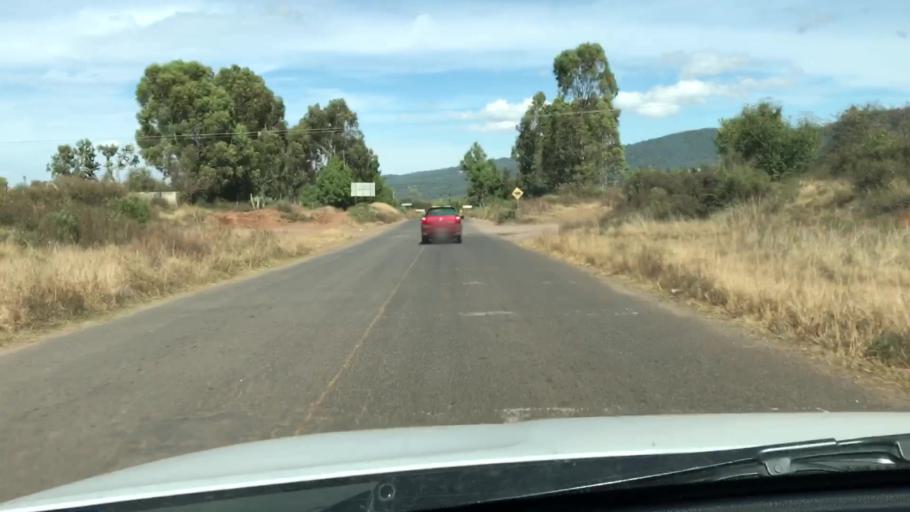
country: MX
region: Jalisco
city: Chiquilistlan
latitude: 20.1322
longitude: -103.7189
